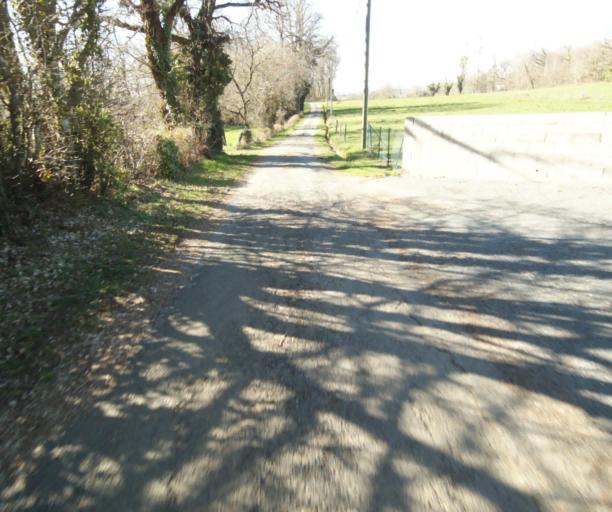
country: FR
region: Limousin
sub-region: Departement de la Correze
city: Chamboulive
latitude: 45.4063
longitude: 1.6590
